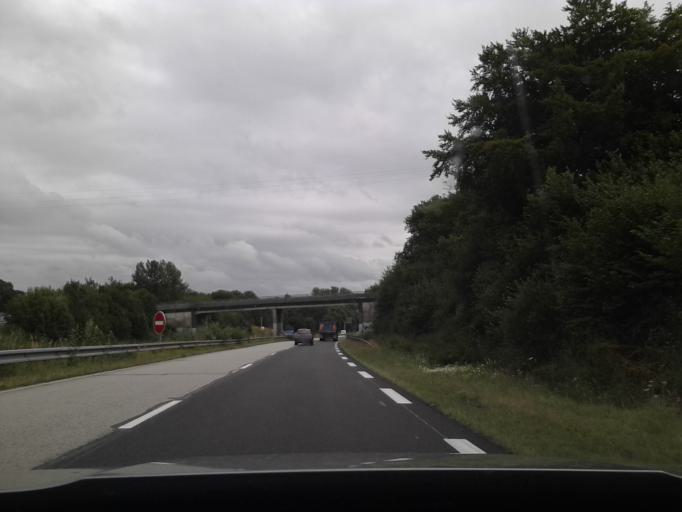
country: FR
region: Lower Normandy
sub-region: Departement de la Manche
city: Brix
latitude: 49.5649
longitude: -1.5697
